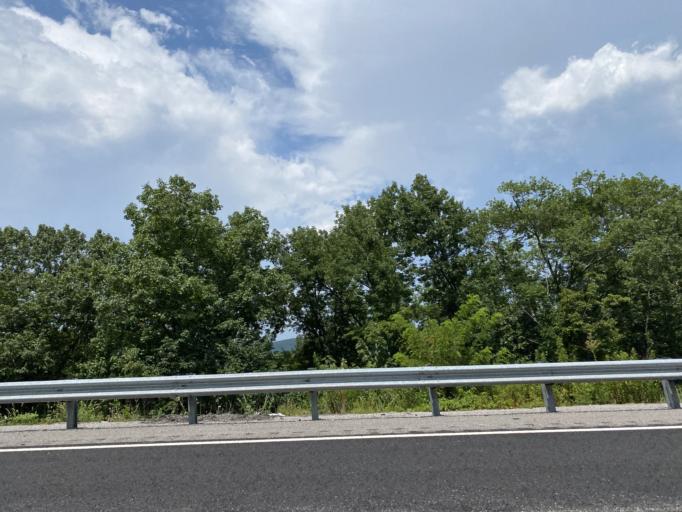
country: US
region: Alabama
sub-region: Madison County
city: Huntsville
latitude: 34.7047
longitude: -86.5201
